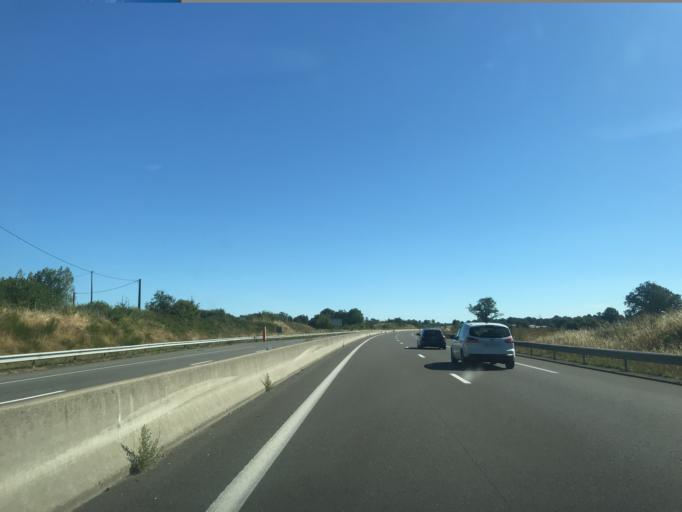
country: FR
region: Limousin
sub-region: Departement de la Creuse
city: Chambon-sur-Voueize
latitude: 46.2879
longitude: 2.4078
